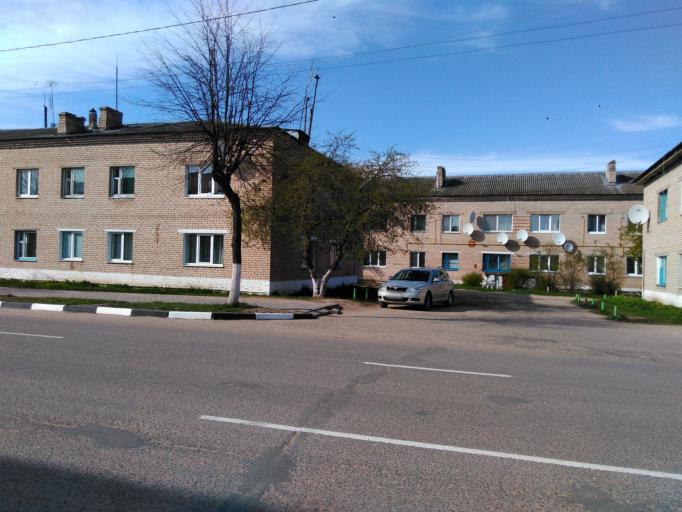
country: BY
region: Vitebsk
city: Chashniki
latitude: 54.8599
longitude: 29.1619
